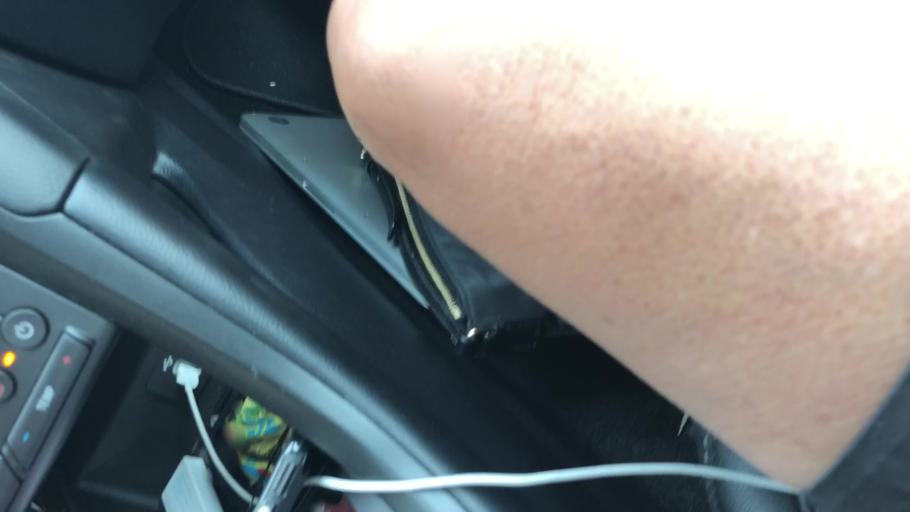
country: US
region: California
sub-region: El Dorado County
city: South Lake Tahoe
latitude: 38.8195
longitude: -120.0273
